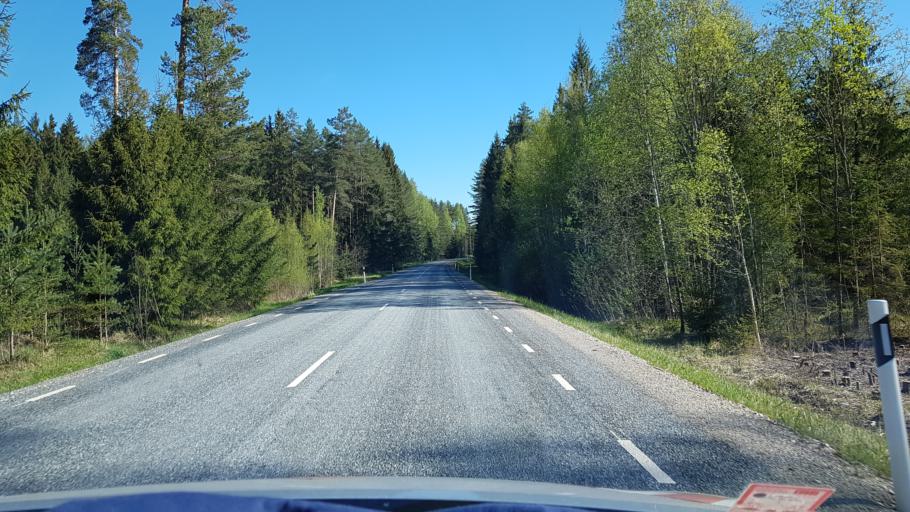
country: EE
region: Polvamaa
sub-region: Polva linn
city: Polva
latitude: 58.1371
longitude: 27.1588
